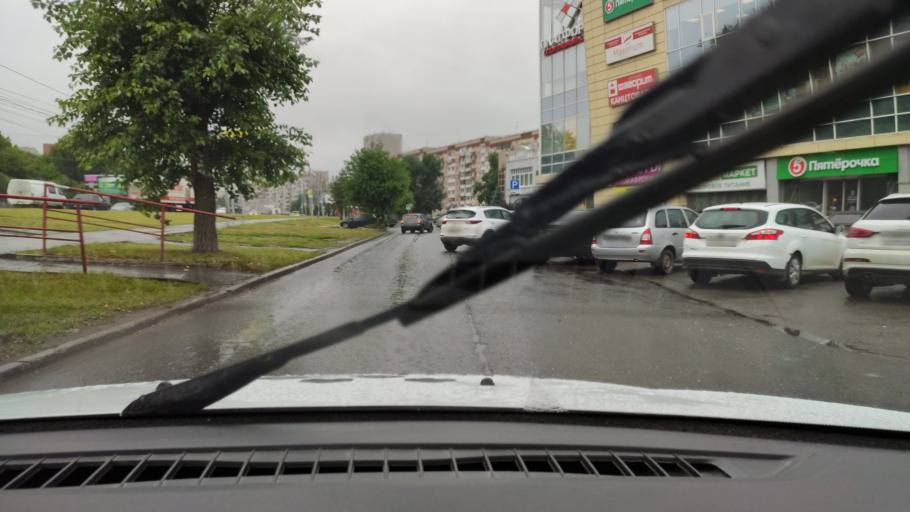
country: RU
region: Udmurtiya
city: Izhevsk
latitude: 56.8791
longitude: 53.2229
